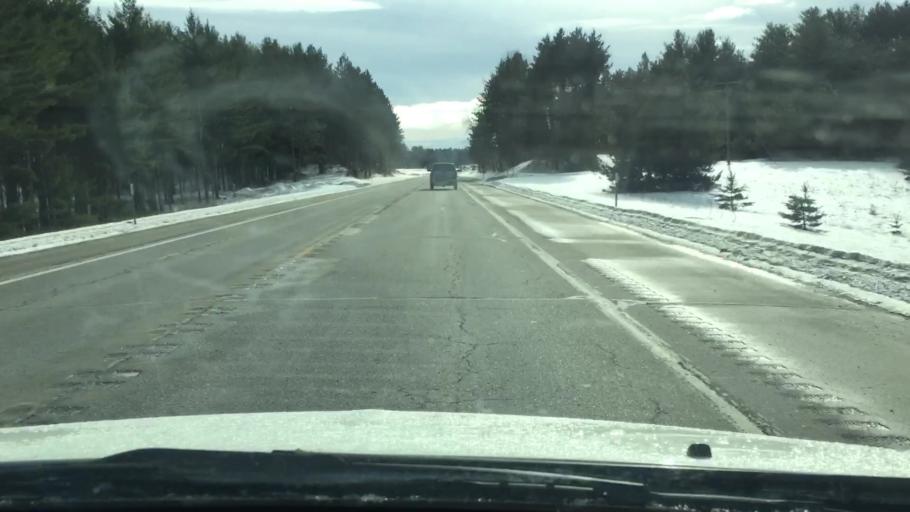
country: US
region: Michigan
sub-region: Kalkaska County
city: Kalkaska
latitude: 44.6363
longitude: -85.2888
